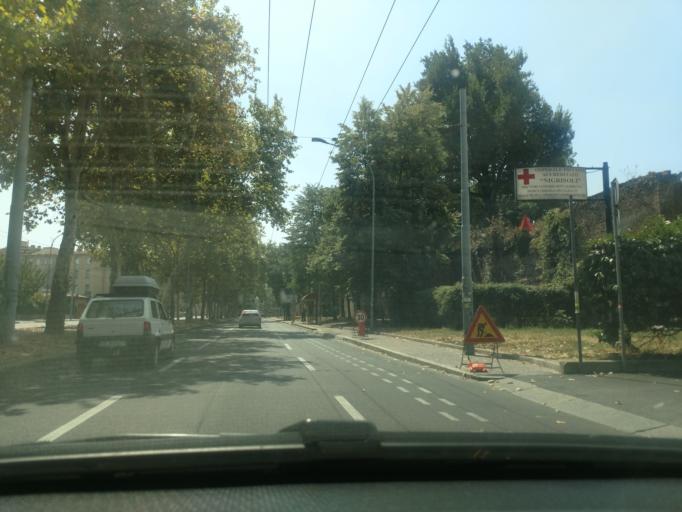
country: IT
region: Emilia-Romagna
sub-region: Provincia di Bologna
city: Bologna
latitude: 44.4923
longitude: 11.3572
